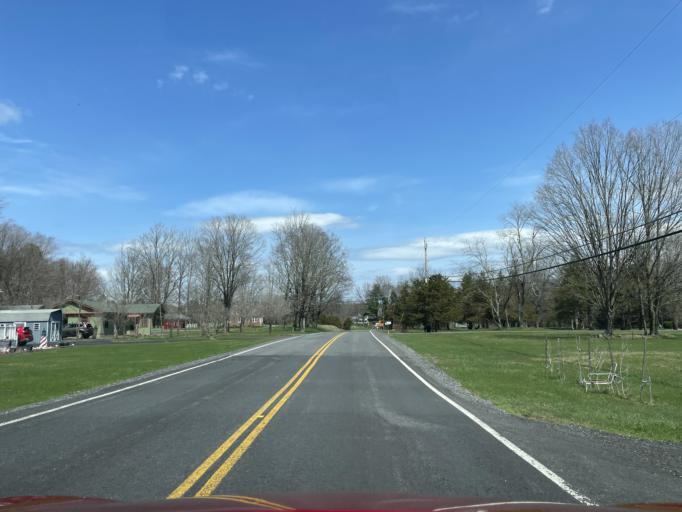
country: US
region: New York
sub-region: Ulster County
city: Manorville
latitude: 42.1338
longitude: -74.0166
